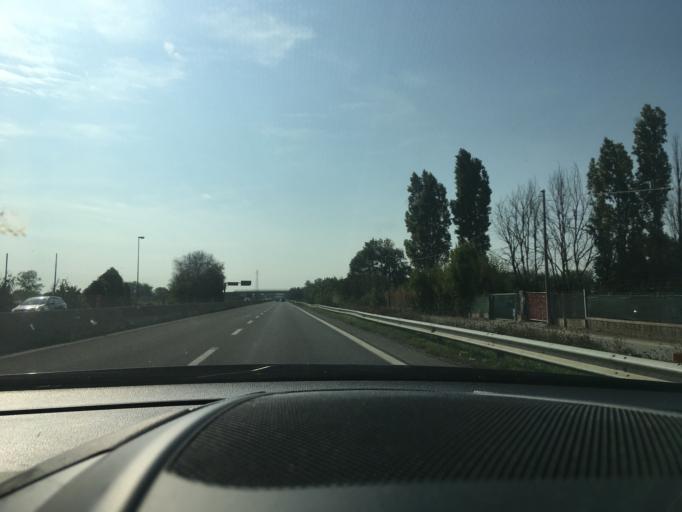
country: IT
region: Emilia-Romagna
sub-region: Provincia di Rimini
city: Bellaria-Igea Marina
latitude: 44.1399
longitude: 12.4591
